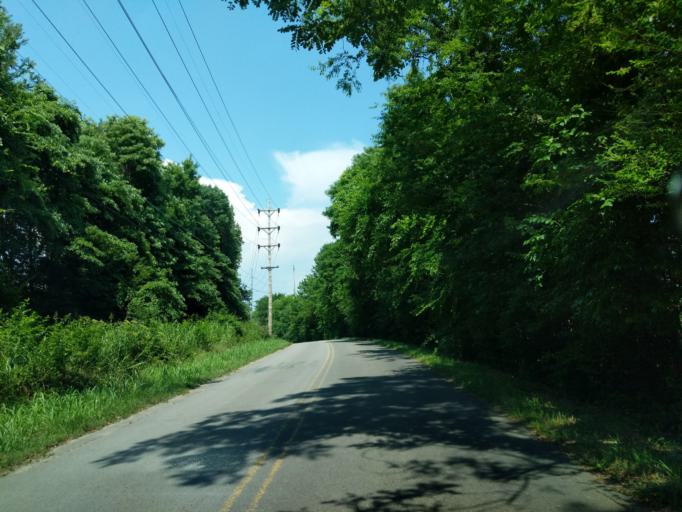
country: US
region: Tennessee
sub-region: Sumner County
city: Hendersonville
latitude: 36.2853
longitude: -86.6710
